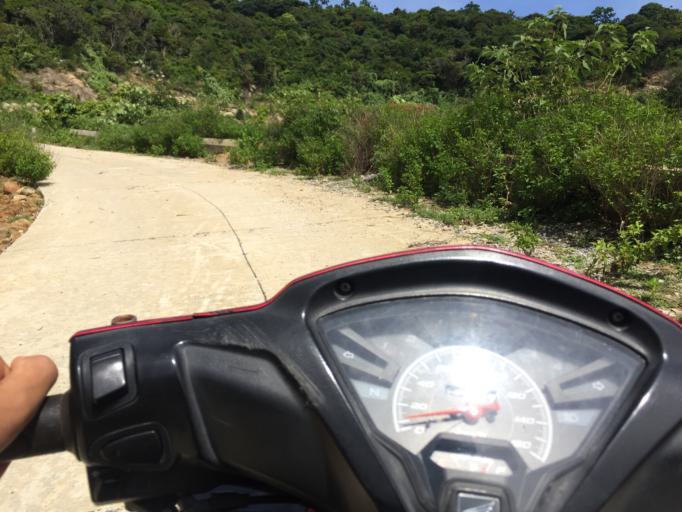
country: VN
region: Quang Nam
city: Hoi An
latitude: 15.9709
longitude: 108.5068
